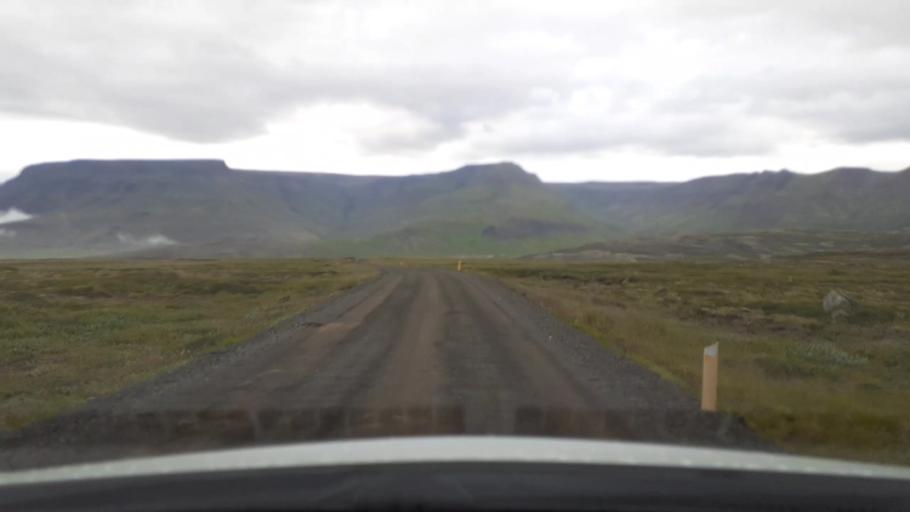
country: IS
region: Capital Region
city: Mosfellsbaer
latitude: 64.1928
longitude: -21.5420
